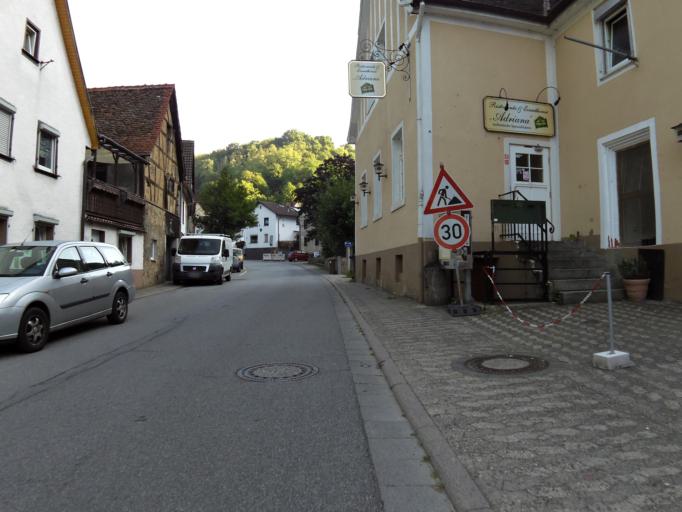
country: DE
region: Hesse
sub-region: Regierungsbezirk Darmstadt
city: Heppenheim an der Bergstrasse
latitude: 49.6529
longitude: 8.6507
